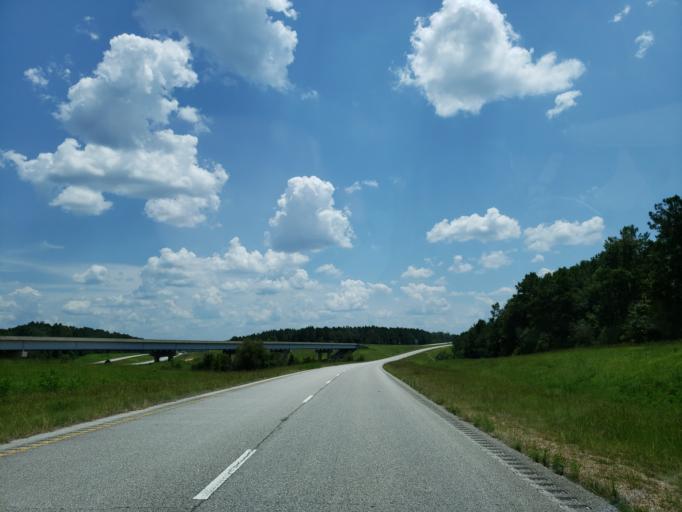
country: US
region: Mississippi
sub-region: Wayne County
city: Belmont
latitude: 31.4551
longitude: -88.4660
